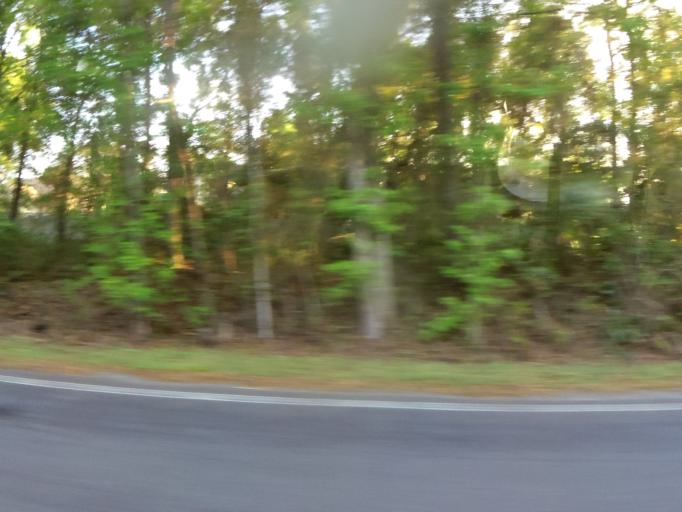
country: US
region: Florida
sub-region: Saint Johns County
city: Fruit Cove
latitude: 30.1250
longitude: -81.5955
